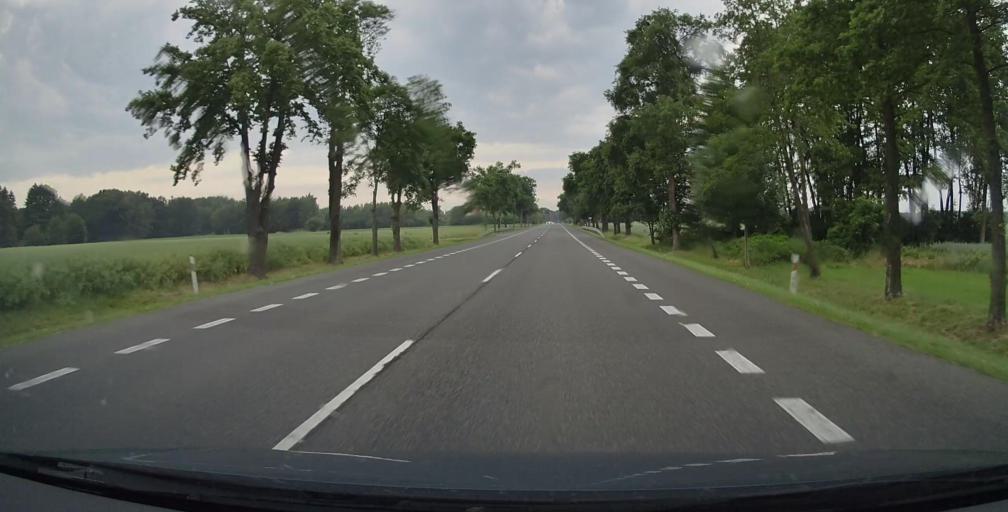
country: PL
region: Lublin Voivodeship
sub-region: Powiat lukowski
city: Trzebieszow
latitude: 52.0654
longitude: 22.5402
